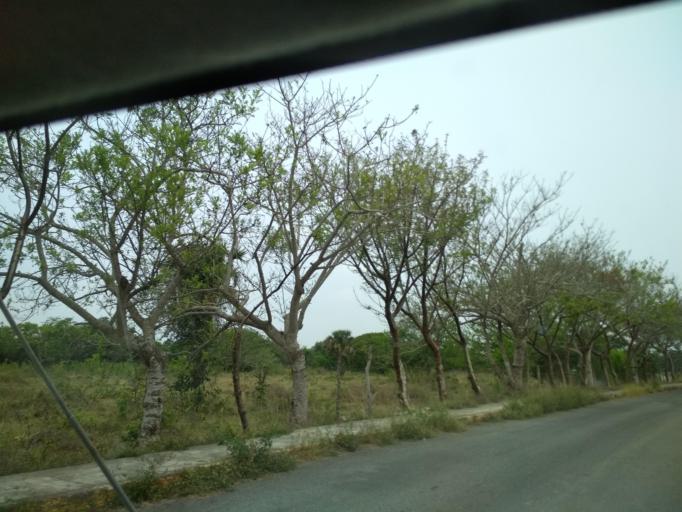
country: MX
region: Veracruz
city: Paso del Toro
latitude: 19.0454
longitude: -96.1488
